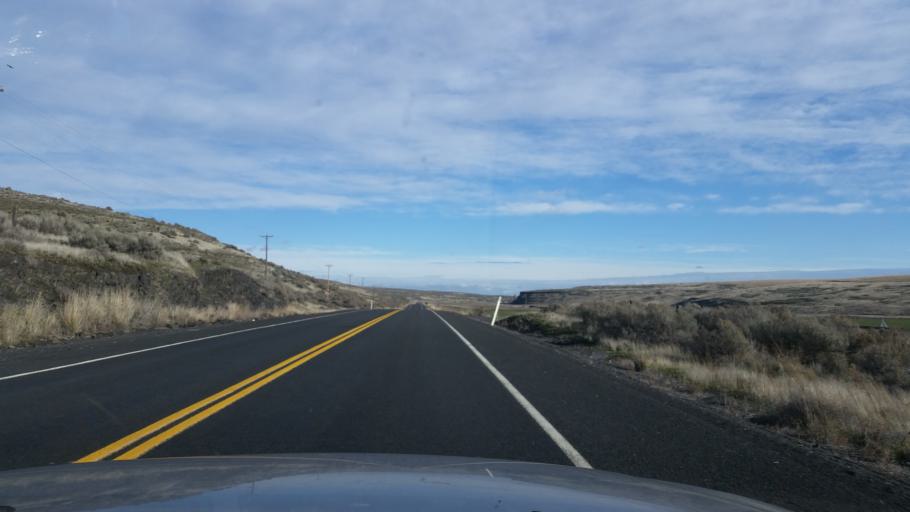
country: US
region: Washington
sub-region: Adams County
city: Ritzville
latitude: 47.3521
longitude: -118.5380
